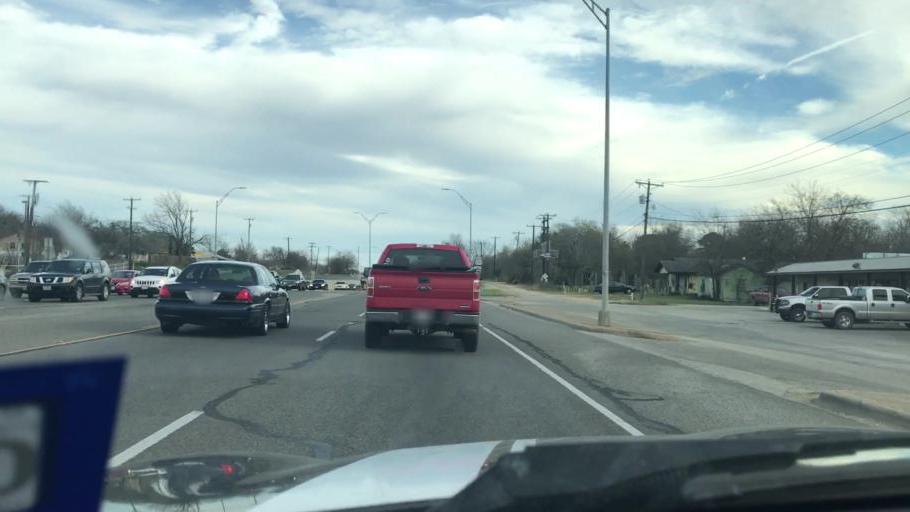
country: US
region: Texas
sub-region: Bastrop County
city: Elgin
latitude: 30.3372
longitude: -97.3704
